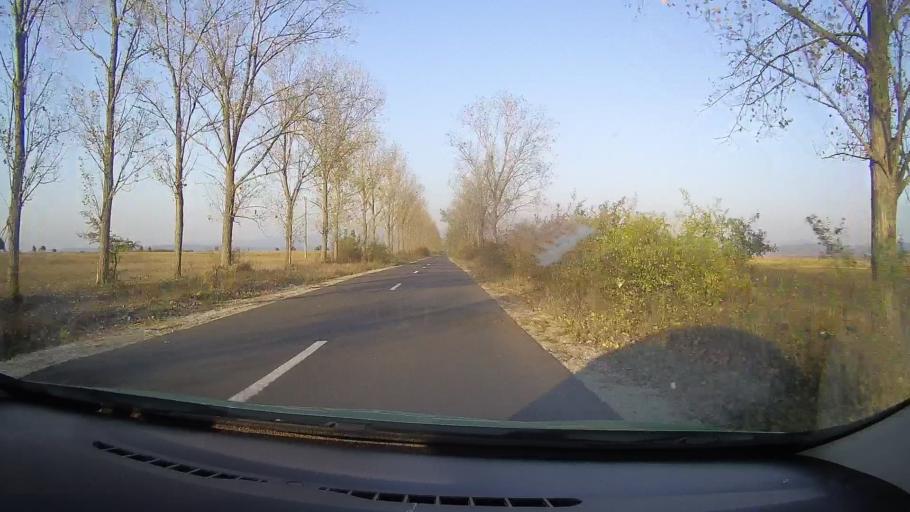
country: RO
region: Arad
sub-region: Comuna Barsa
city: Barsa
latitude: 46.3645
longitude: 22.0368
